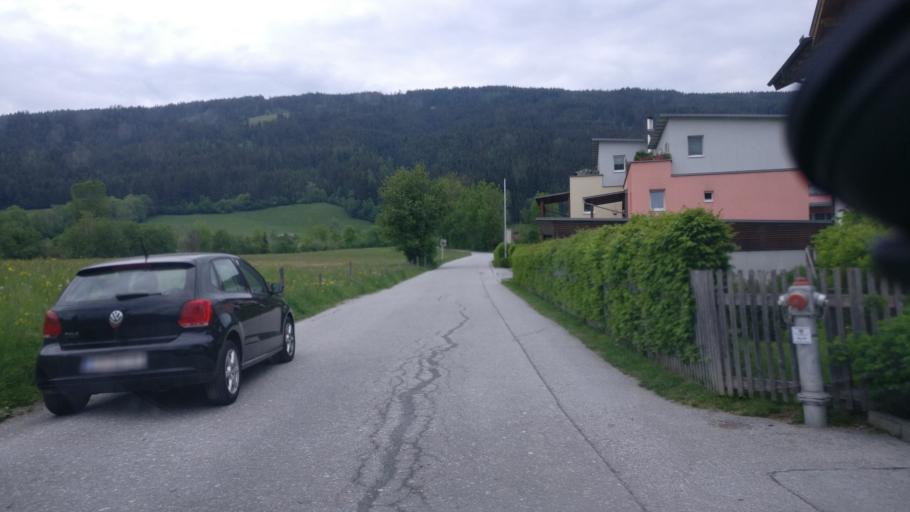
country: AT
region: Salzburg
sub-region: Politischer Bezirk Sankt Johann im Pongau
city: Radstadt
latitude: 47.3834
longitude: 13.4486
